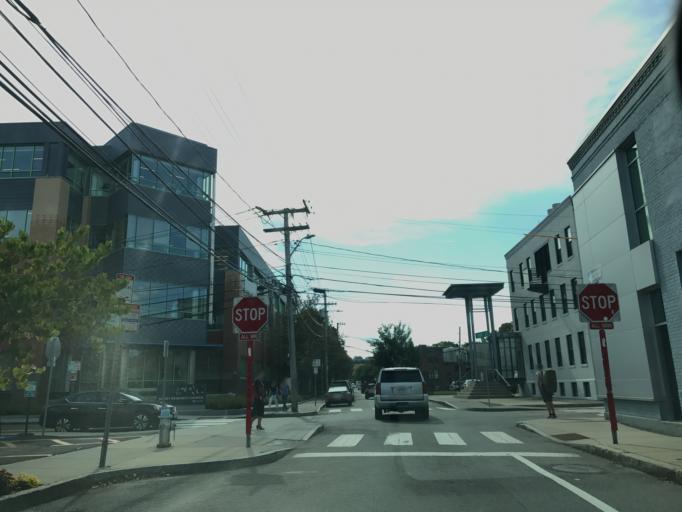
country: US
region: Massachusetts
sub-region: Middlesex County
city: Cambridge
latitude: 42.3586
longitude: -71.1047
